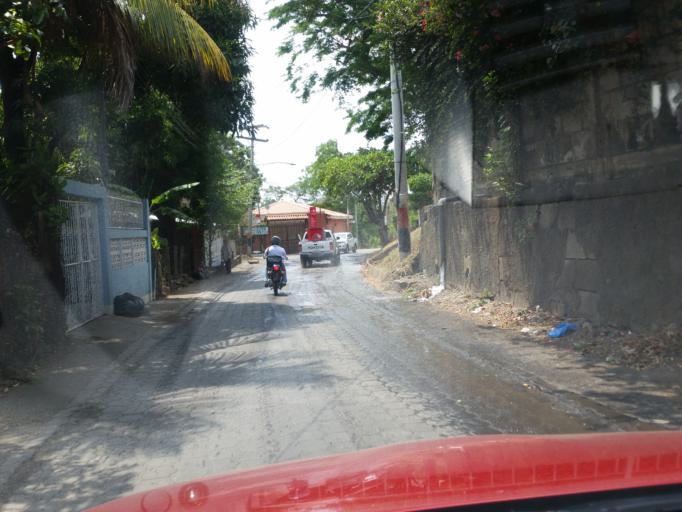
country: NI
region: Managua
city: Managua
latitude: 12.0844
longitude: -86.2390
